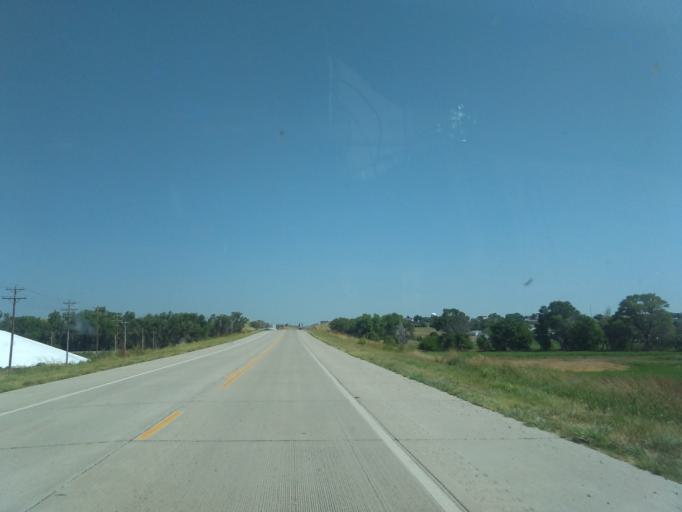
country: US
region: Nebraska
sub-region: Dundy County
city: Benkelman
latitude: 40.0395
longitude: -101.5433
